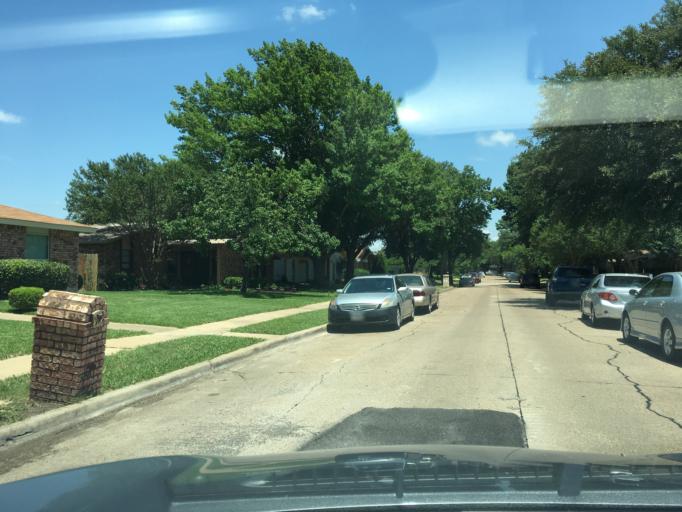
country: US
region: Texas
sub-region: Dallas County
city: Richardson
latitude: 32.9492
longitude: -96.6812
